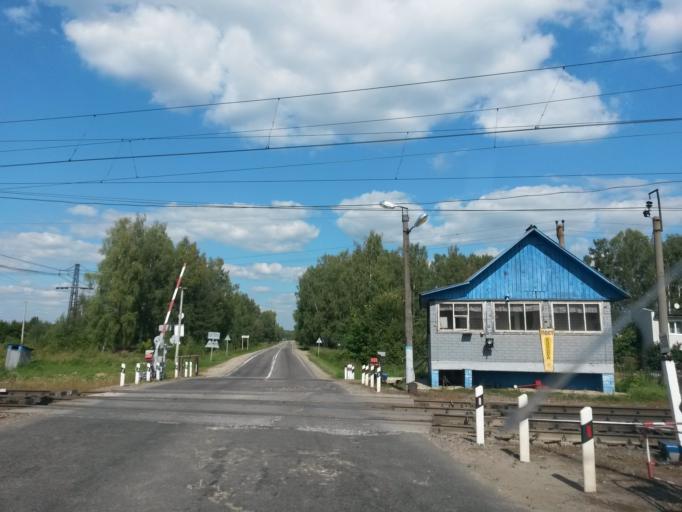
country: RU
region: Jaroslavl
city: Tunoshna
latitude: 57.4932
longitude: 40.1154
